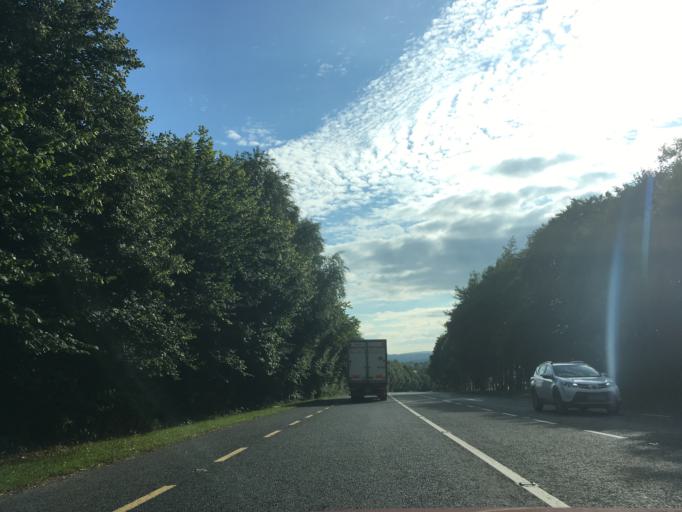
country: IE
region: Leinster
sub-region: Loch Garman
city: New Ross
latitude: 52.3843
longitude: -6.9286
